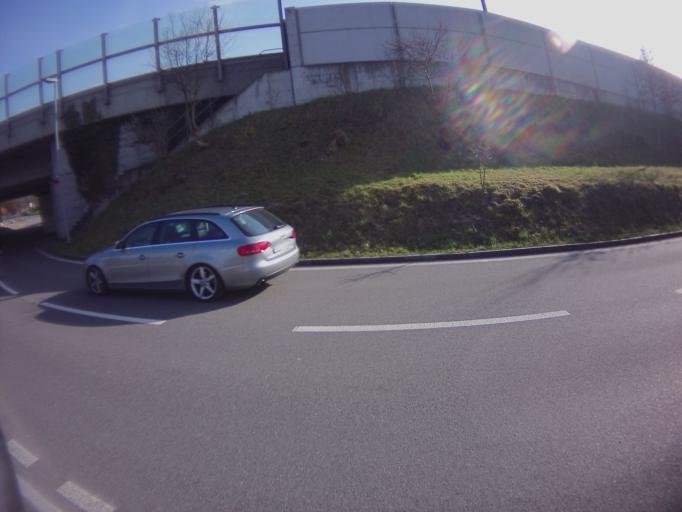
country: CH
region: Aargau
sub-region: Bezirk Baden
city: Neuenhof
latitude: 47.4551
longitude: 8.3289
